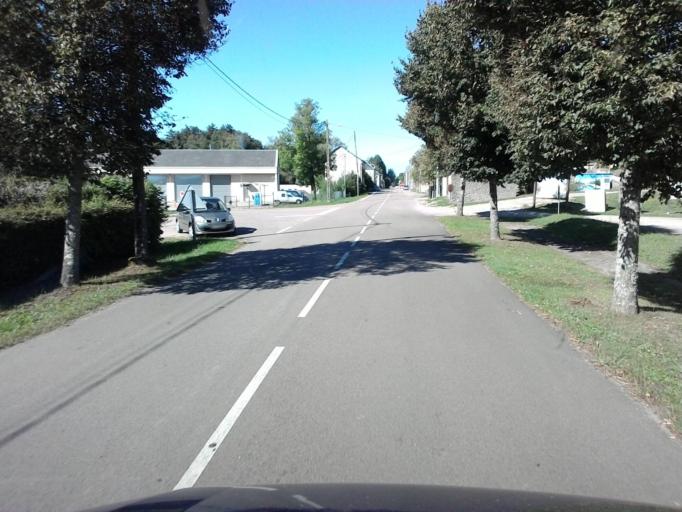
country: FR
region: Bourgogne
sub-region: Departement de la Nievre
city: Lormes
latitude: 47.2814
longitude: 3.8216
